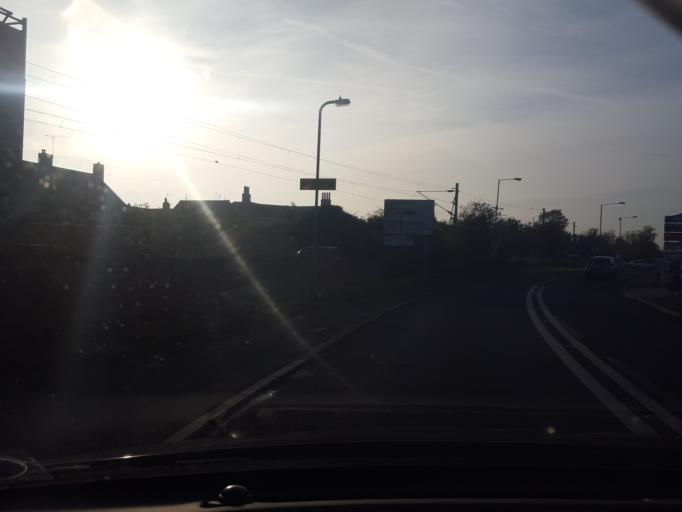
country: GB
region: England
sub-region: Essex
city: Frinton-on-Sea
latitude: 51.8378
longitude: 1.2463
